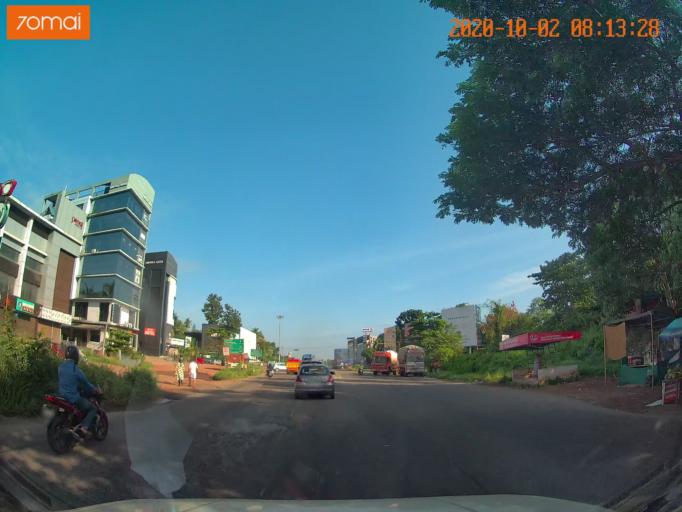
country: IN
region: Kerala
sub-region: Kozhikode
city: Kozhikode
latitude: 11.2863
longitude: 75.8012
